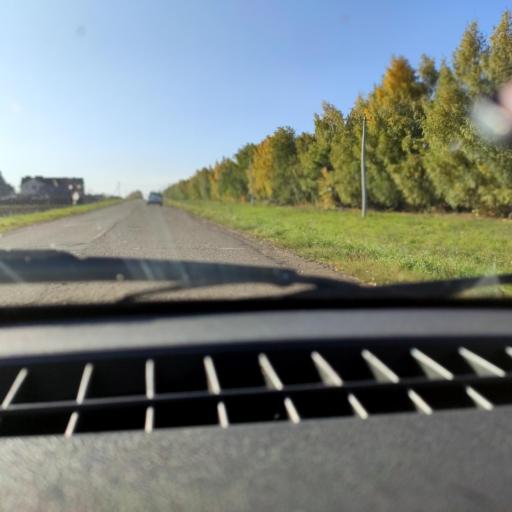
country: RU
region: Bashkortostan
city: Avdon
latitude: 54.5983
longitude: 55.7992
